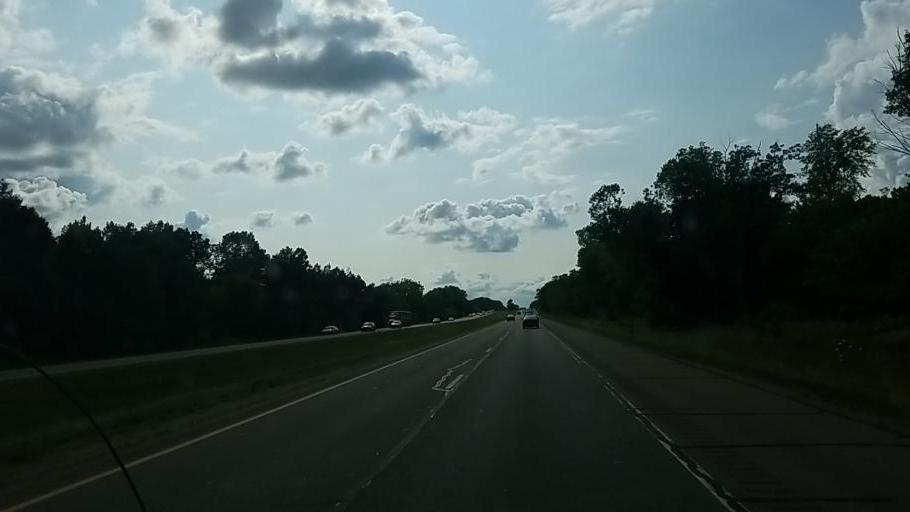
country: US
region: Michigan
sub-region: Ingham County
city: Holt
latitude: 42.6599
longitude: -84.5560
